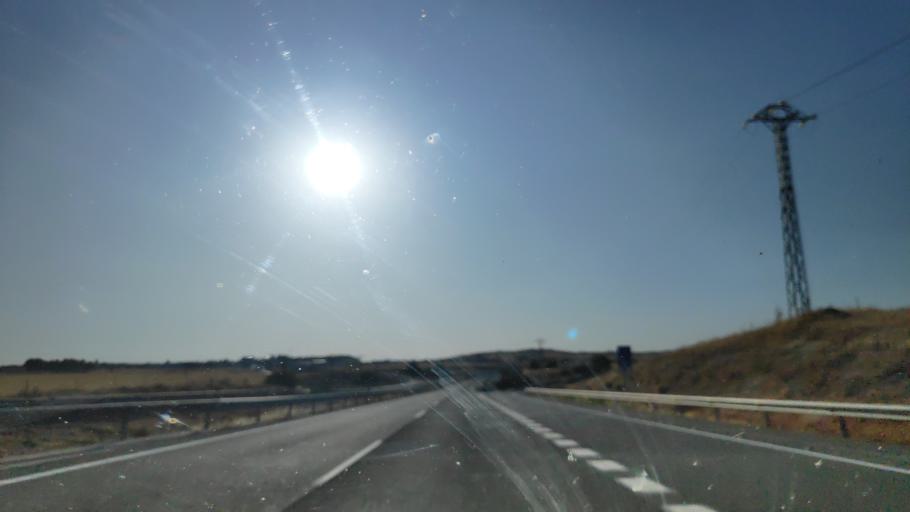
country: ES
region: Castille-La Mancha
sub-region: Provincia de Cuenca
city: Montalbo
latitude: 39.8808
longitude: -2.6492
